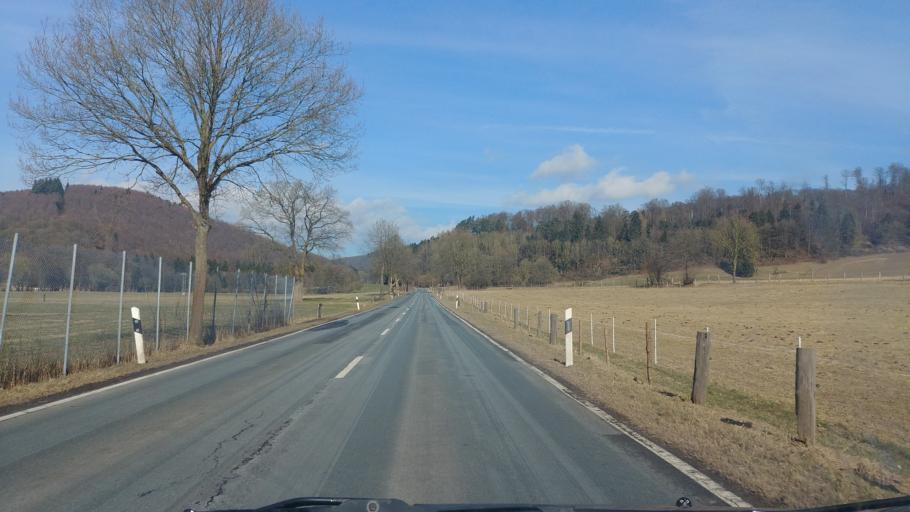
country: DE
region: Lower Saxony
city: Bodenfelde
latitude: 51.6527
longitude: 9.5481
